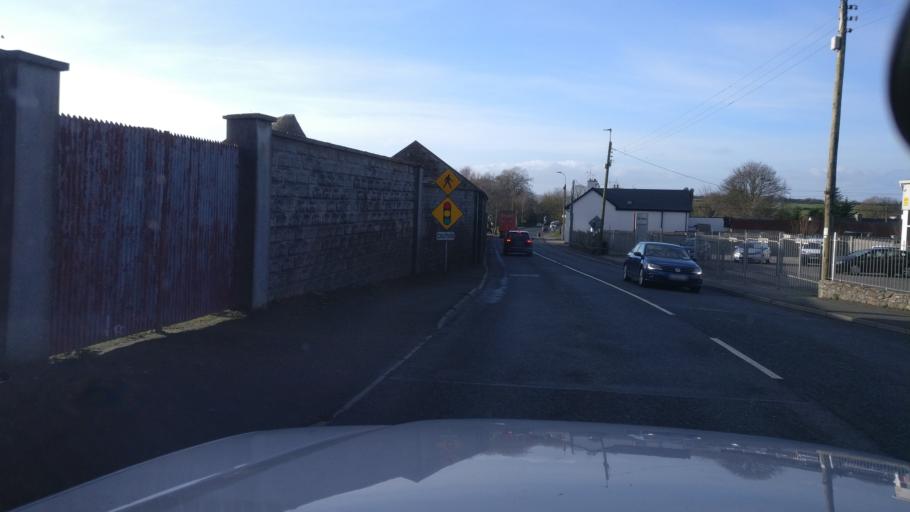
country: IE
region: Leinster
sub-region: Uibh Fhaili
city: Tullamore
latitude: 53.2138
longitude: -7.4479
